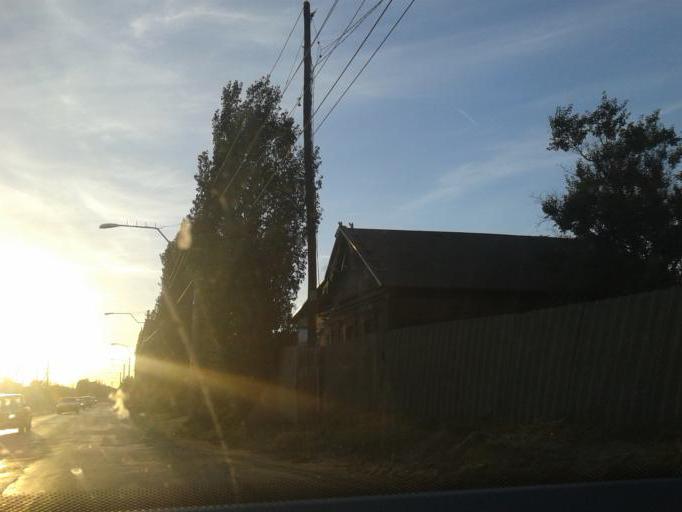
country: RU
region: Volgograd
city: Krasnoslobodsk
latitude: 48.7074
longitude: 44.5848
